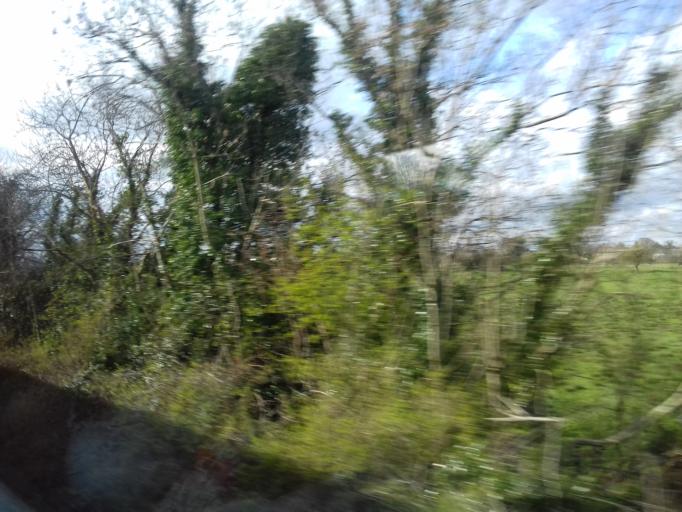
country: IE
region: Leinster
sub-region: An Iarmhi
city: Kinnegad
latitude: 53.4746
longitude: -7.0276
